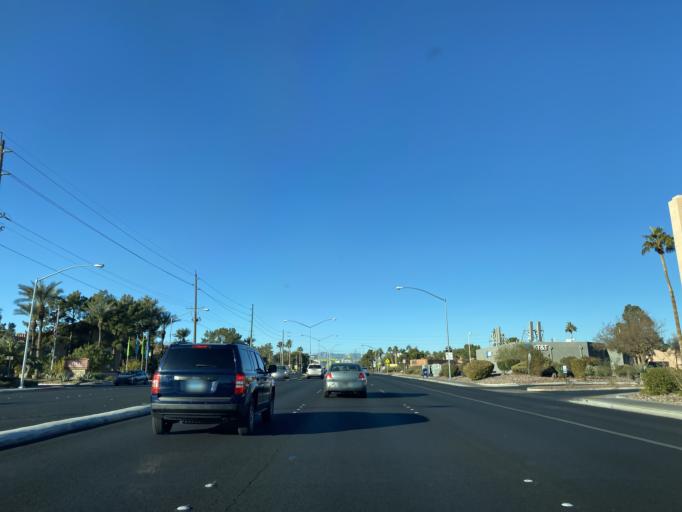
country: US
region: Nevada
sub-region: Clark County
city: Winchester
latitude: 36.1153
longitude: -115.1026
